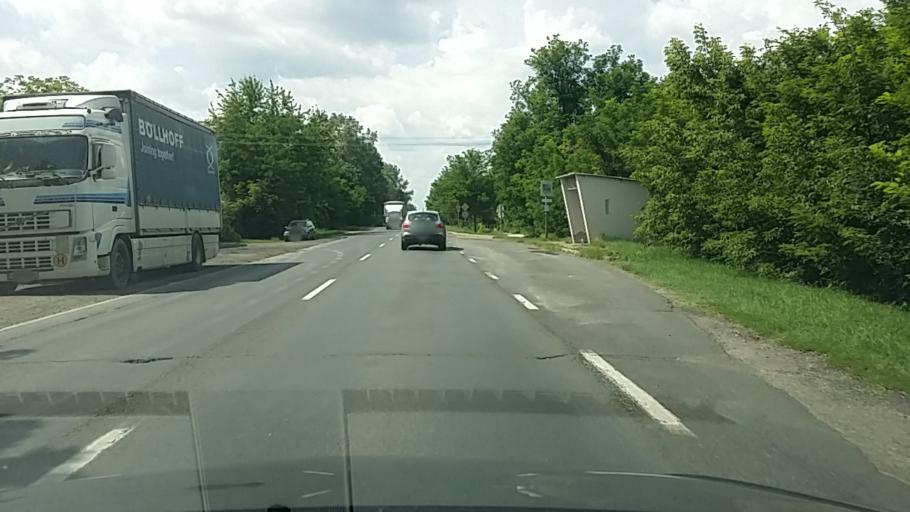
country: HU
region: Bacs-Kiskun
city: Lajosmizse
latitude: 46.9972
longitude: 19.6000
